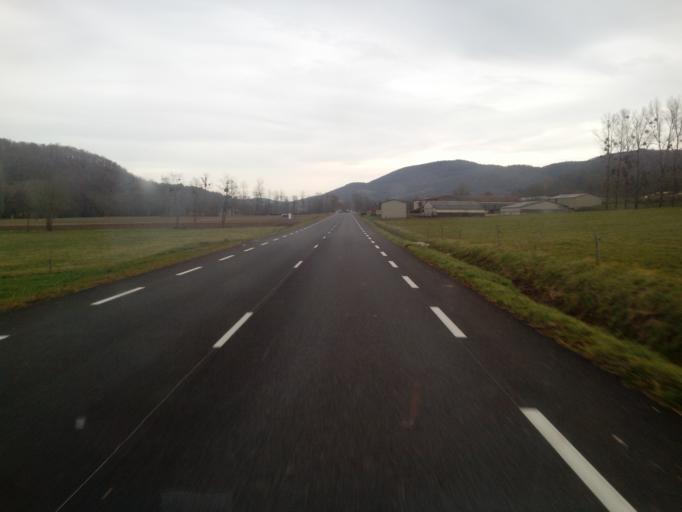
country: FR
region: Midi-Pyrenees
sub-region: Departement de l'Ariege
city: Foix
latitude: 43.0109
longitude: 1.4468
